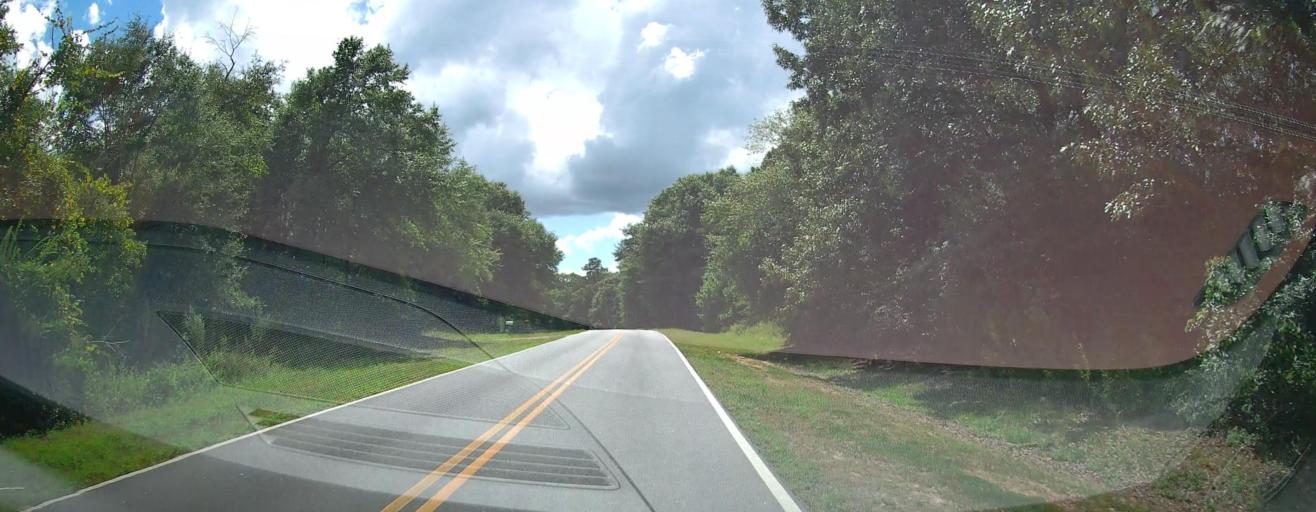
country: US
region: Georgia
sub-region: Chattahoochee County
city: Cusseta
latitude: 32.3066
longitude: -84.7662
